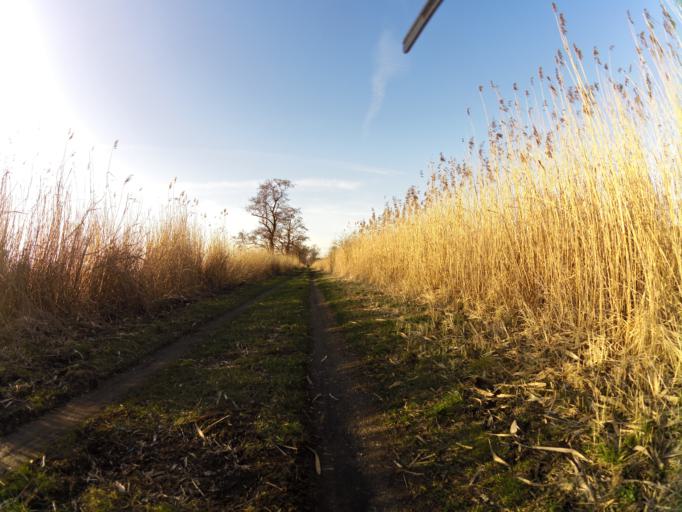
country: PL
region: West Pomeranian Voivodeship
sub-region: Powiat policki
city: Nowe Warpno
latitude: 53.7293
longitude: 14.3047
